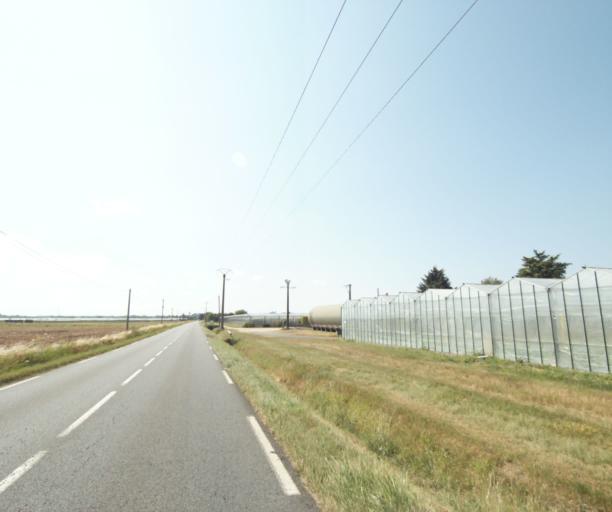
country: FR
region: Centre
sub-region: Departement du Loiret
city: Saint-Cyr-en-Val
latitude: 47.8498
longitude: 1.9552
